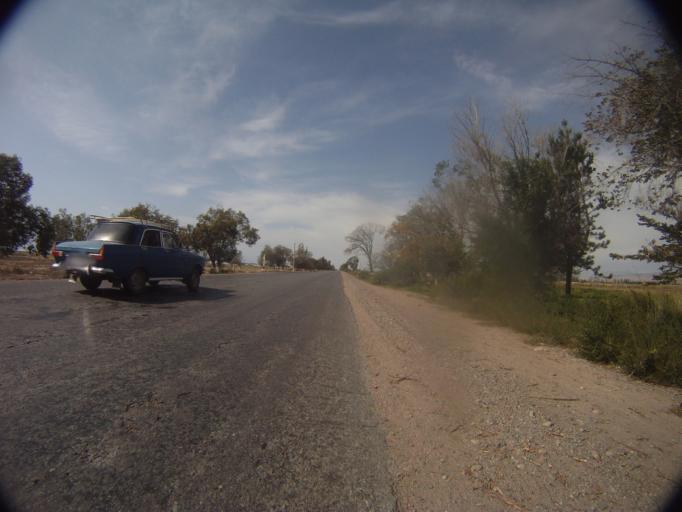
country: KG
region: Ysyk-Koel
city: Cholpon-Ata
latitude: 42.5743
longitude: 76.6874
